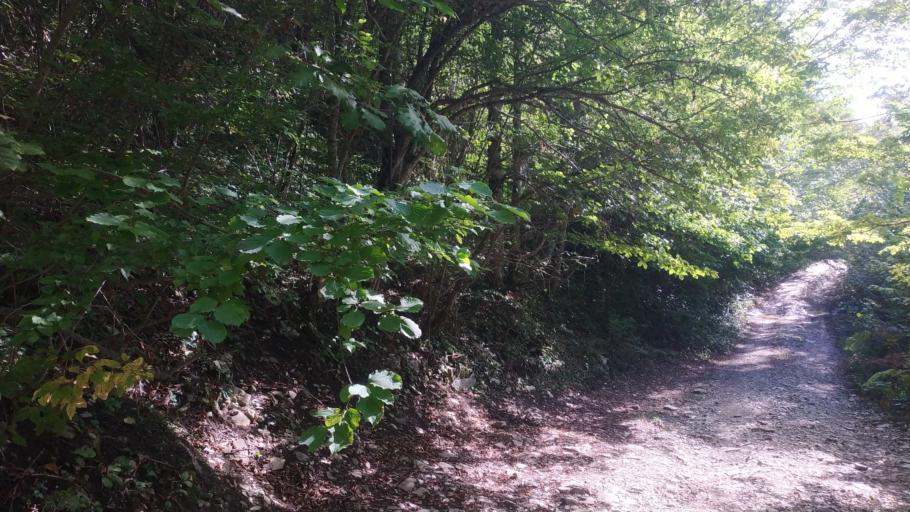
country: RU
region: Krasnodarskiy
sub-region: Sochi City
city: Lazarevskoye
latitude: 43.9845
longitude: 39.4071
